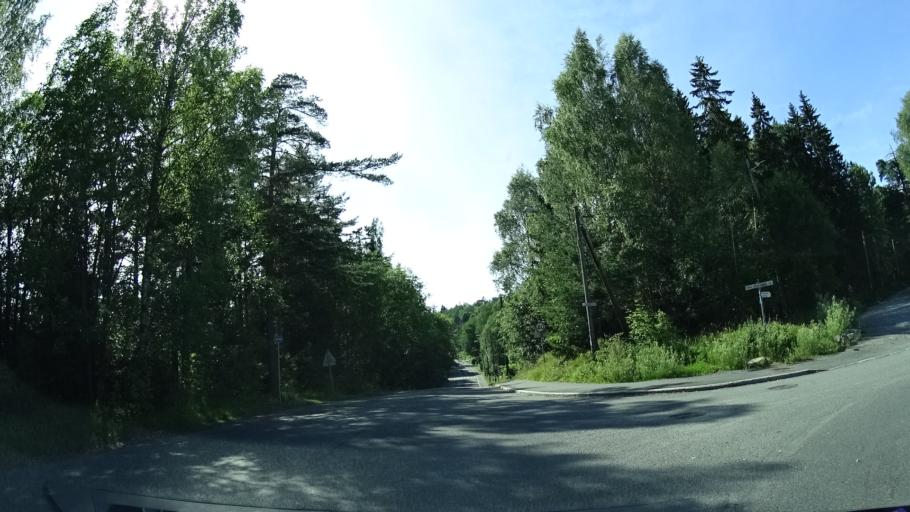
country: NO
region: Oslo
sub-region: Oslo
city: Sjolyststranda
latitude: 59.9594
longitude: 10.6856
